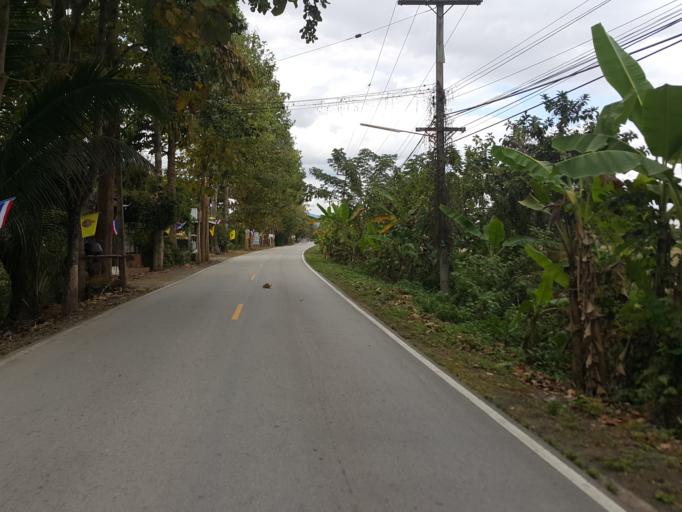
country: TH
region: Chiang Mai
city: San Sai
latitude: 18.8461
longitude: 99.1468
